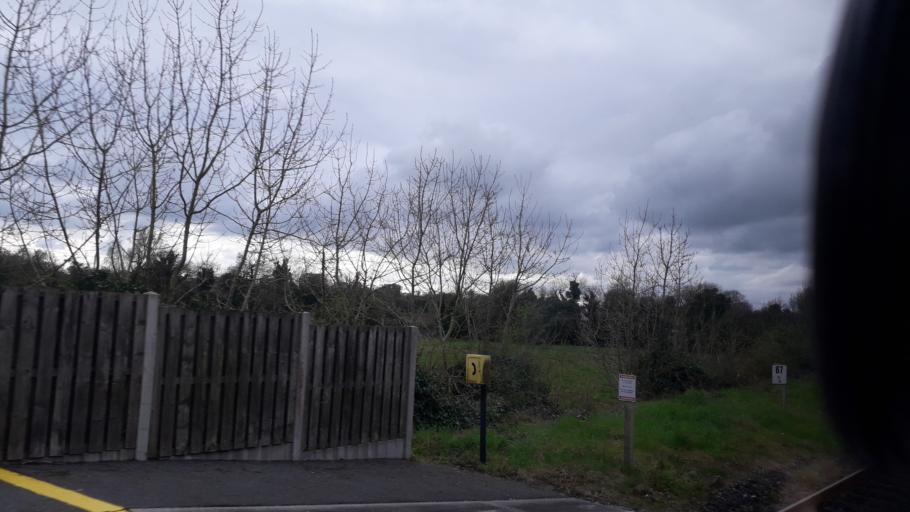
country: IE
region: Leinster
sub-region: An Longfort
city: Edgeworthstown
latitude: 53.6891
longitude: -7.6050
